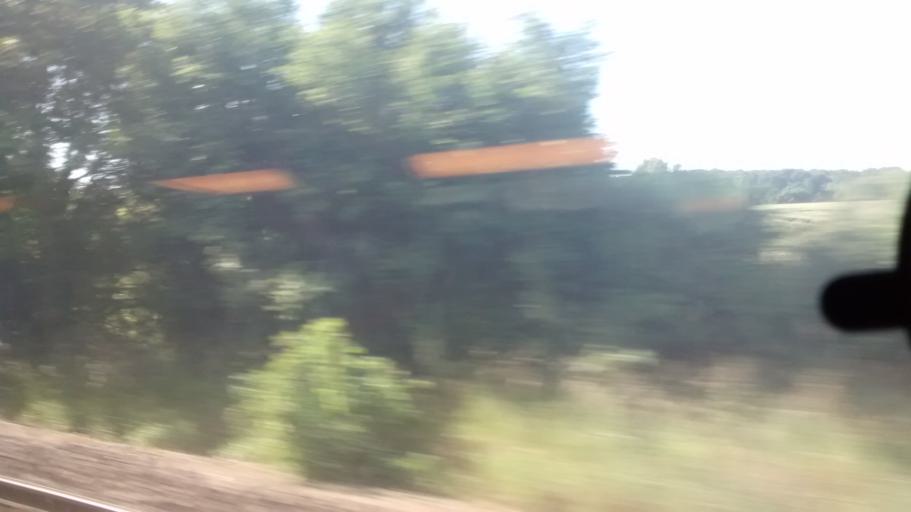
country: FR
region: Pays de la Loire
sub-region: Departement de la Sarthe
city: Aigne
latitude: 48.1025
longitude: 0.0553
